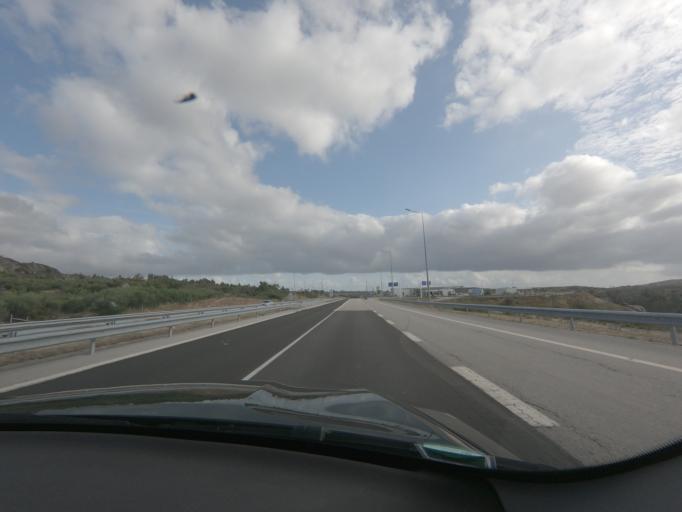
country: PT
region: Viseu
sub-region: Castro Daire
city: Castro Daire
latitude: 40.9694
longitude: -7.8891
